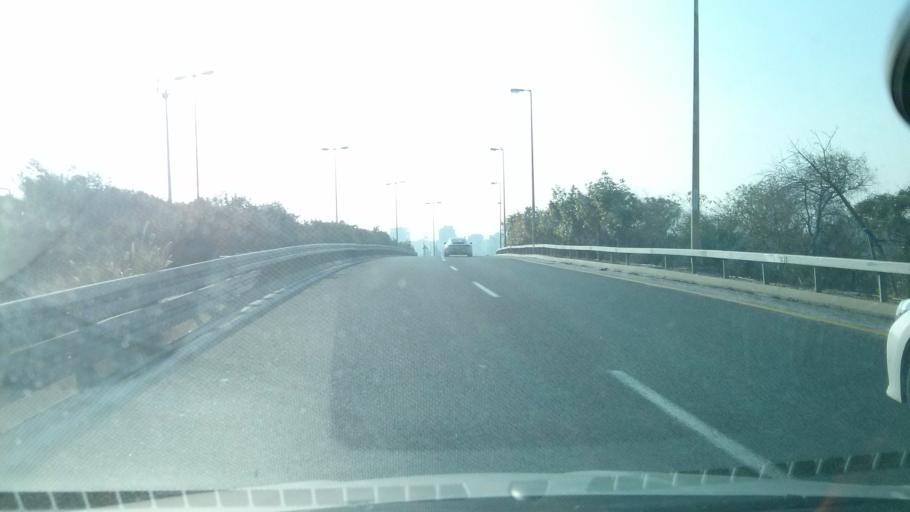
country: IL
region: Tel Aviv
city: Herzliyya
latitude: 32.1396
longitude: 34.8085
